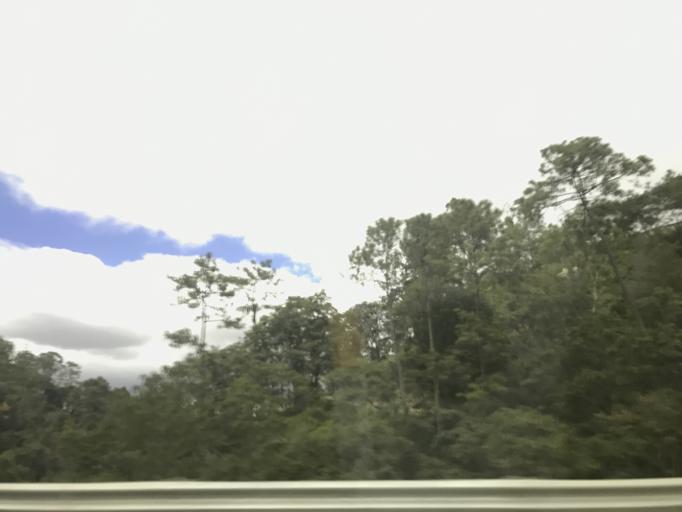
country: GT
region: Chimaltenango
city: El Tejar
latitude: 14.6387
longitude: -90.7925
